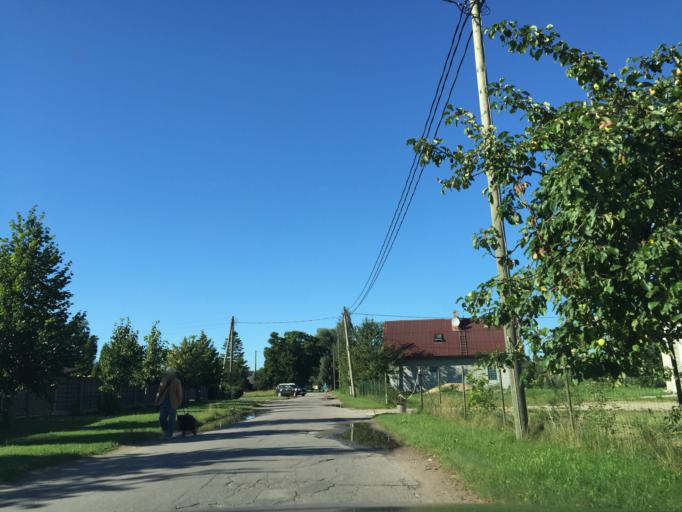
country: LV
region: Riga
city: Jaunciems
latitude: 57.0565
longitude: 24.1382
